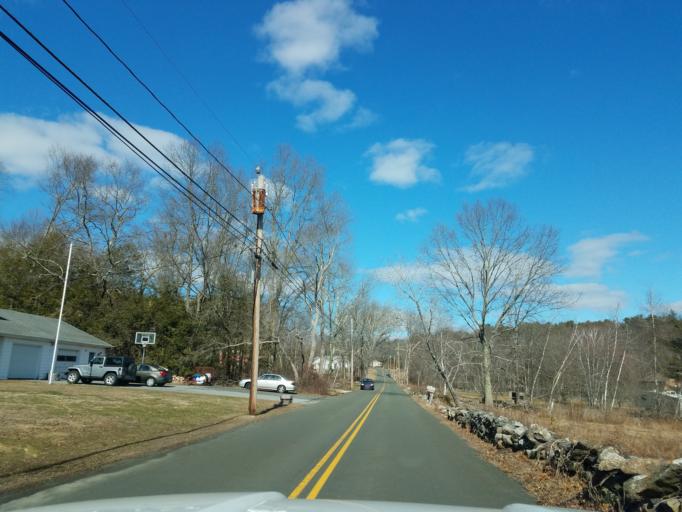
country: US
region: Connecticut
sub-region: Windham County
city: North Grosvenor Dale
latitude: 41.9912
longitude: -71.8862
